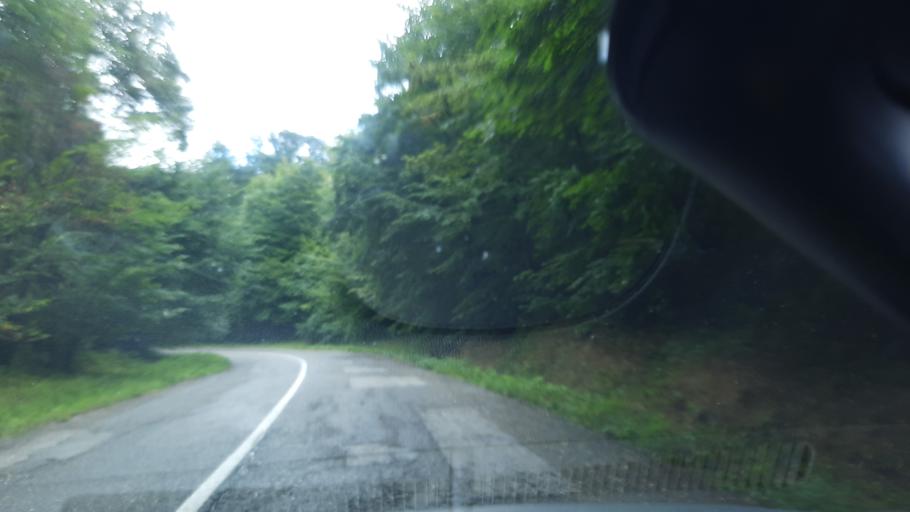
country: RS
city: Glozan
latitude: 45.1537
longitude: 19.5855
